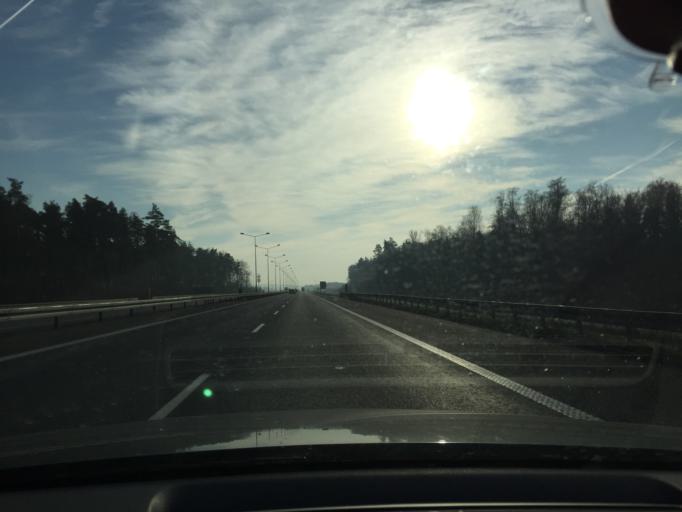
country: PL
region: Silesian Voivodeship
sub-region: Powiat gliwicki
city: Sosnicowice
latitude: 50.3190
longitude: 18.5489
